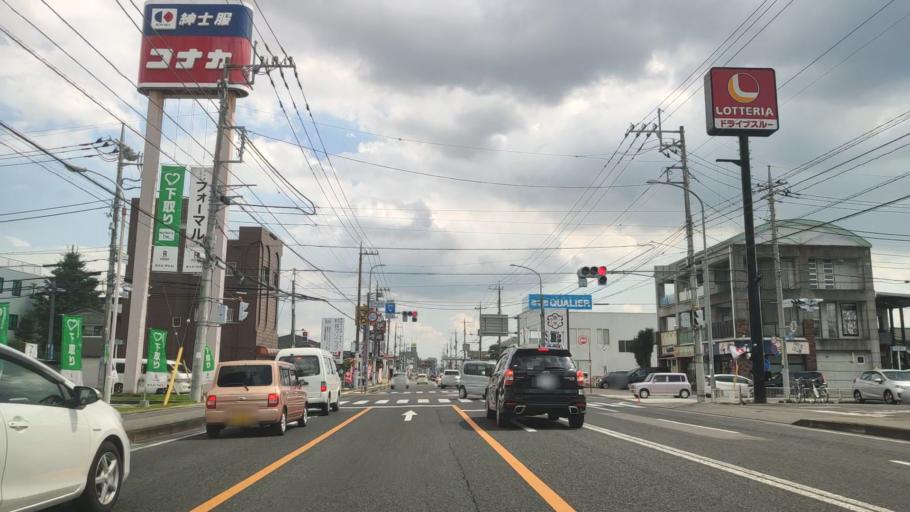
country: JP
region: Tochigi
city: Utsunomiya-shi
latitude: 36.5862
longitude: 139.8658
